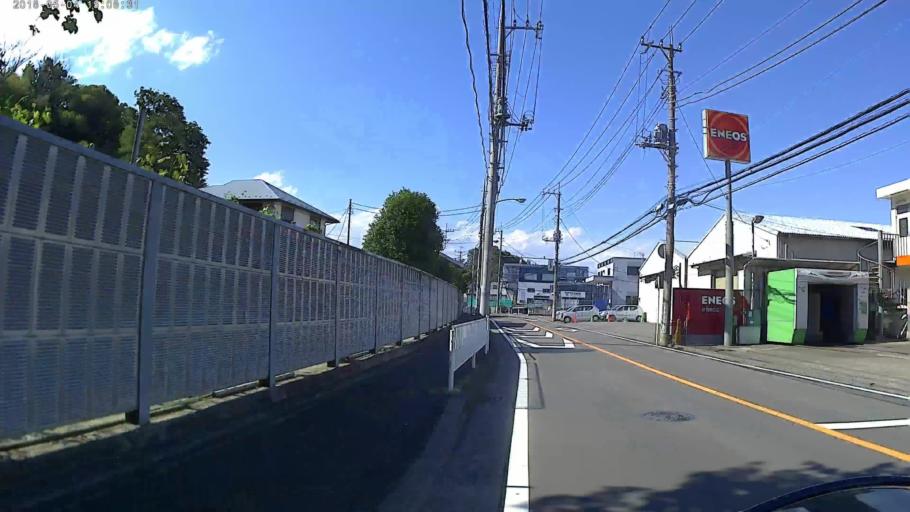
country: JP
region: Kanagawa
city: Yokohama
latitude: 35.5187
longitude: 139.6097
